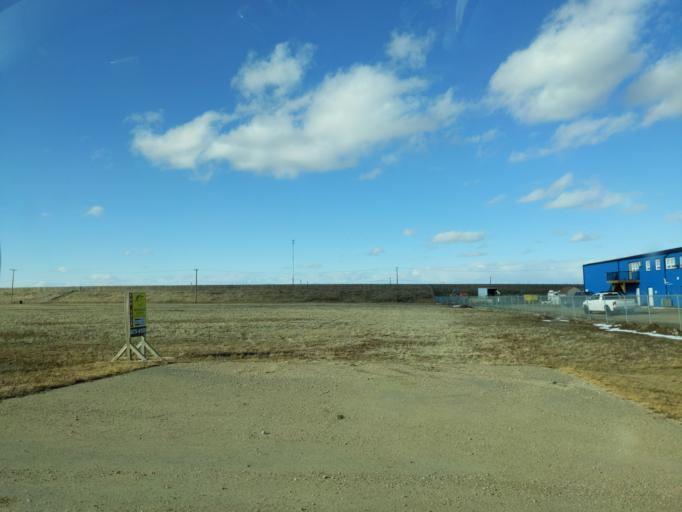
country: CA
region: Saskatchewan
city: Lloydminster
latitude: 53.2440
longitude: -109.9751
